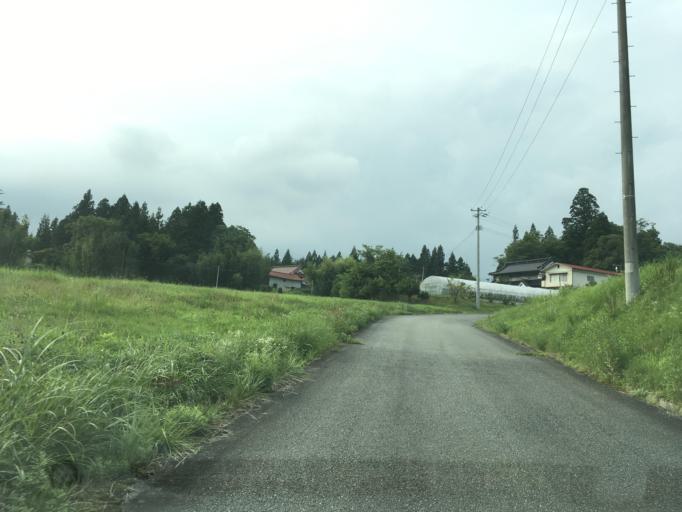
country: JP
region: Iwate
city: Ichinoseki
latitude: 38.9297
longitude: 141.3508
